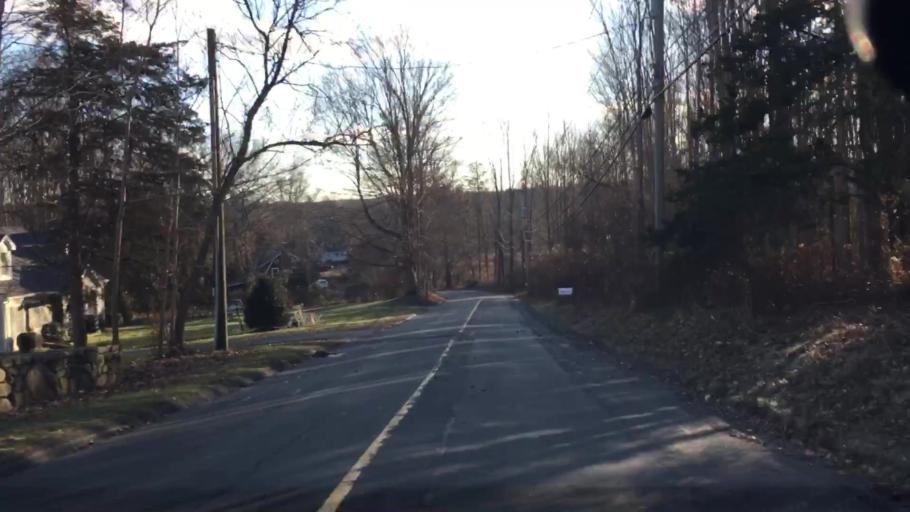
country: US
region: Connecticut
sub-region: Fairfield County
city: Newtown
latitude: 41.4203
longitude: -73.2890
